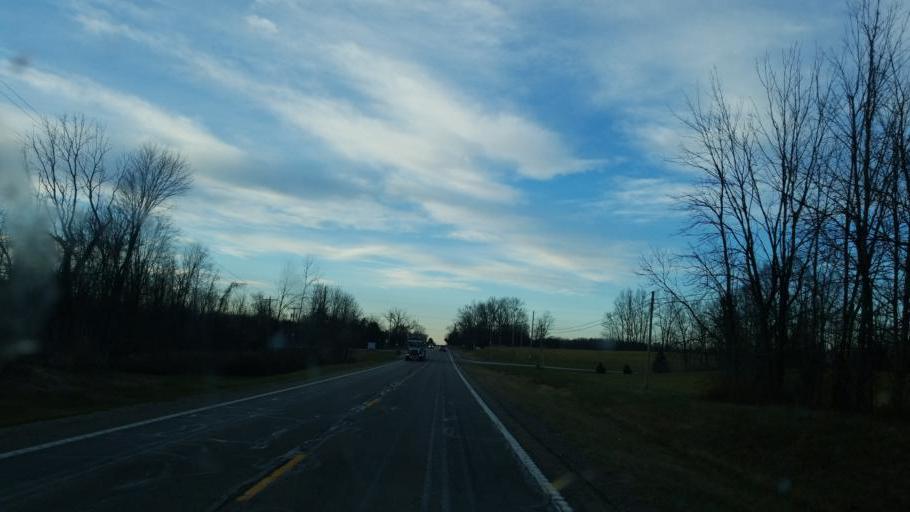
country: US
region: Ohio
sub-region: Morrow County
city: Mount Gilead
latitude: 40.5124
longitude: -82.7404
